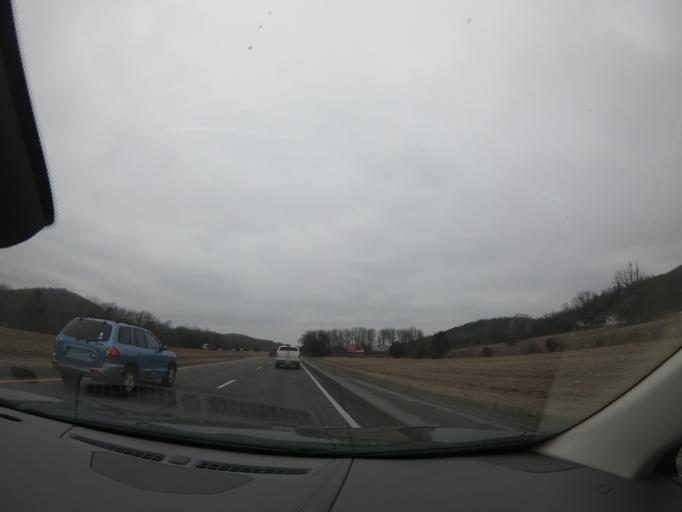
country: US
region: Tennessee
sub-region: Rutherford County
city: Plainview
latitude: 35.6625
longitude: -86.2716
